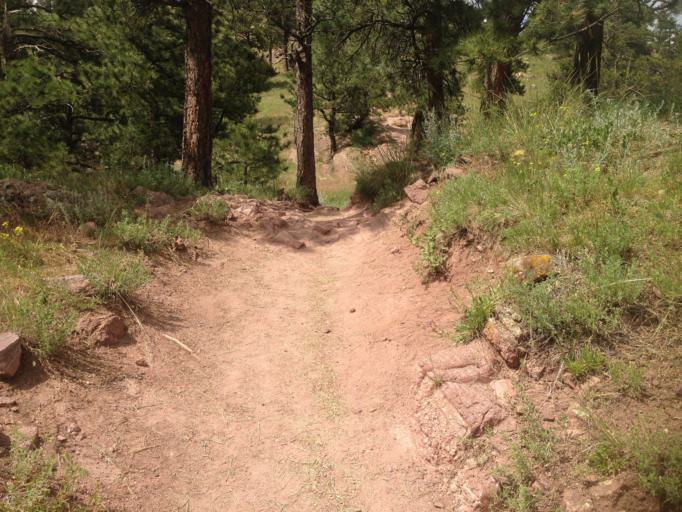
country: US
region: Colorado
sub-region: Boulder County
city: Boulder
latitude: 40.0315
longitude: -105.3043
